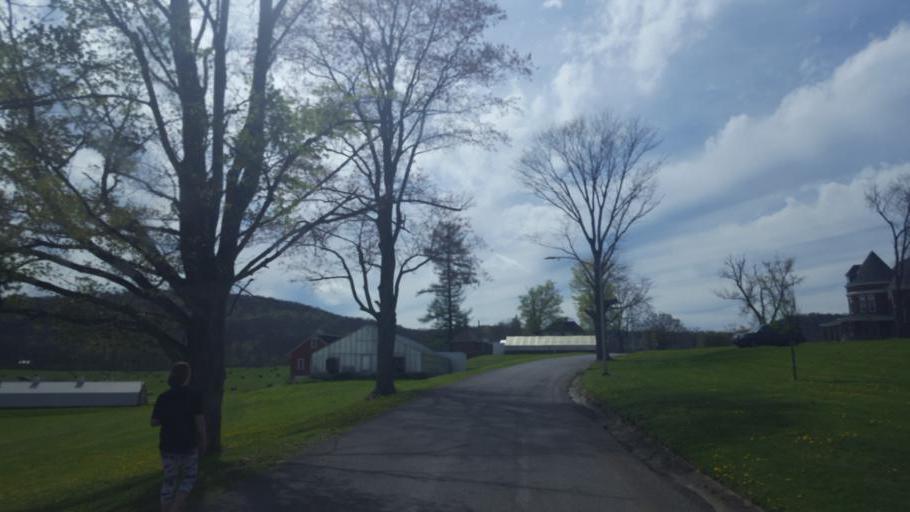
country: US
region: Pennsylvania
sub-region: Venango County
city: Sugarcreek
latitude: 41.3694
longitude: -79.9294
